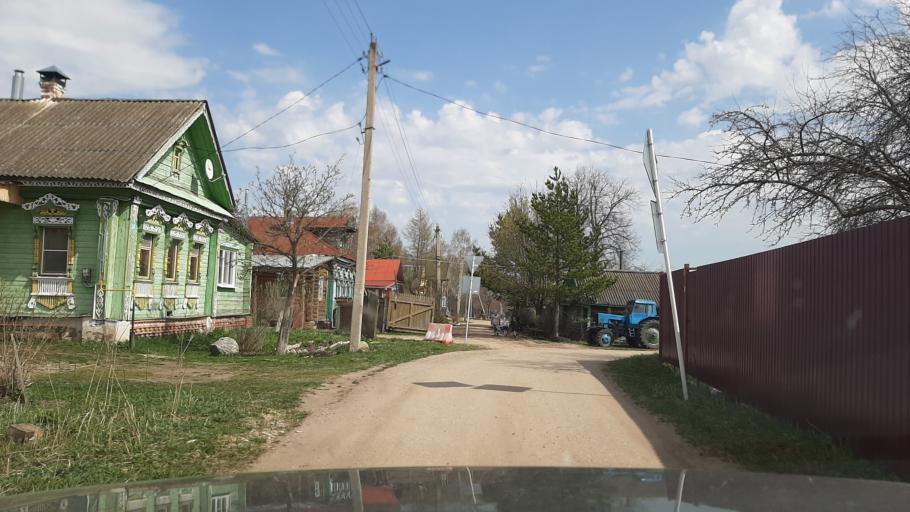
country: RU
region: Ivanovo
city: Furmanov
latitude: 57.3173
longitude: 41.1607
